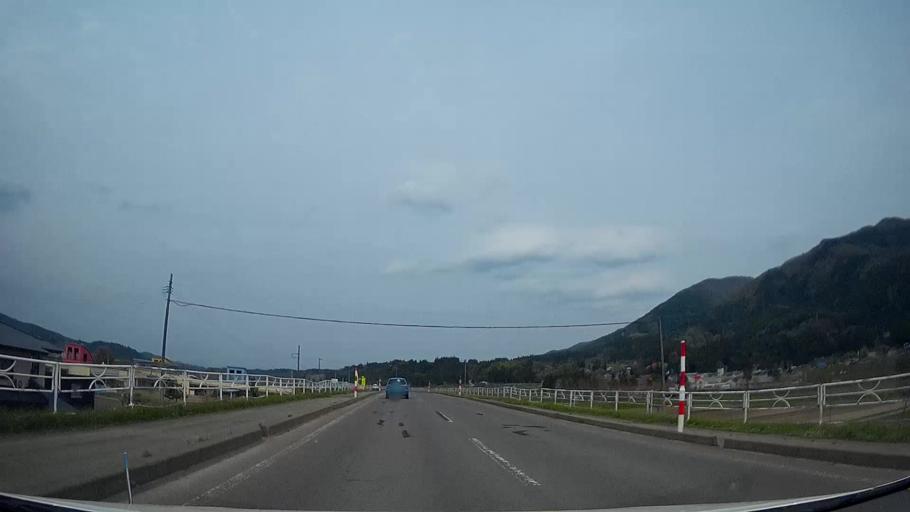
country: JP
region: Akita
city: Hanawa
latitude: 40.1375
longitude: 140.7997
